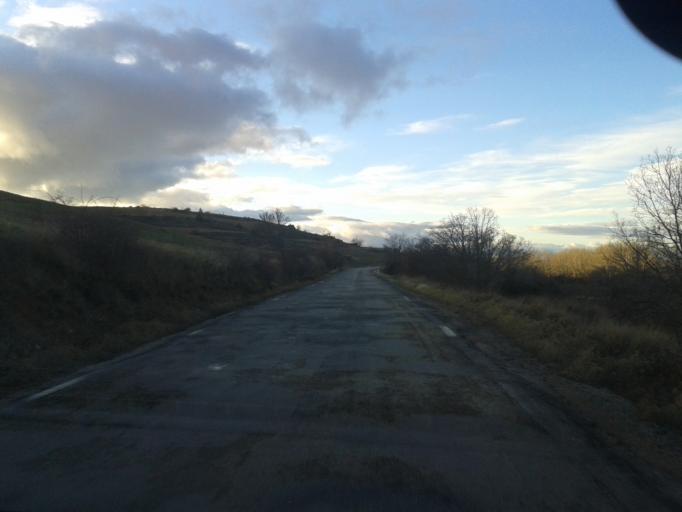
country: ES
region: Aragon
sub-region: Provincia de Teruel
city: Lagueruela
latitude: 41.0405
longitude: -1.2027
